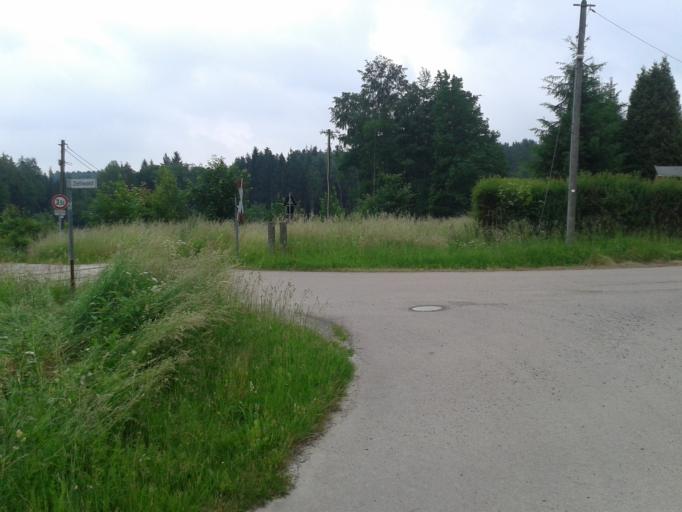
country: DE
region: Saxony
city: Nossen
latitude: 51.0311
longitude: 13.2741
